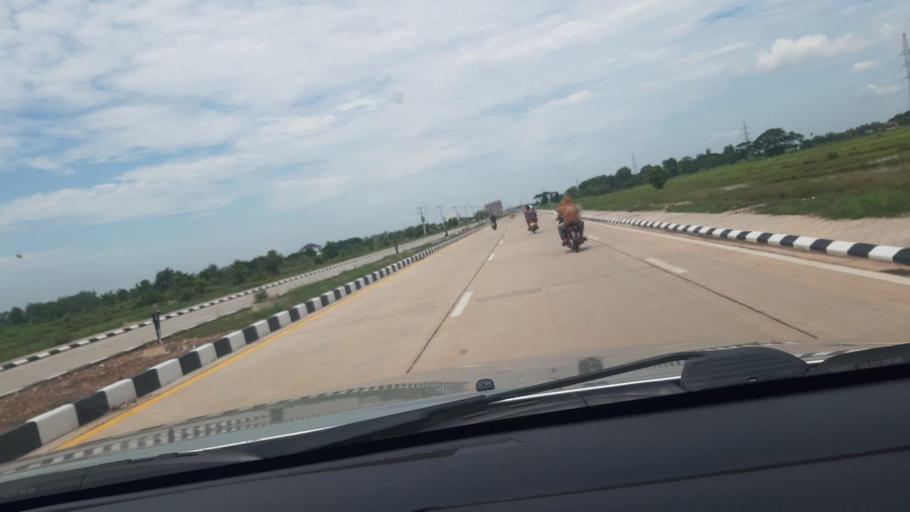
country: LA
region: Vientiane
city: Vientiane
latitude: 18.0219
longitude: 102.5965
